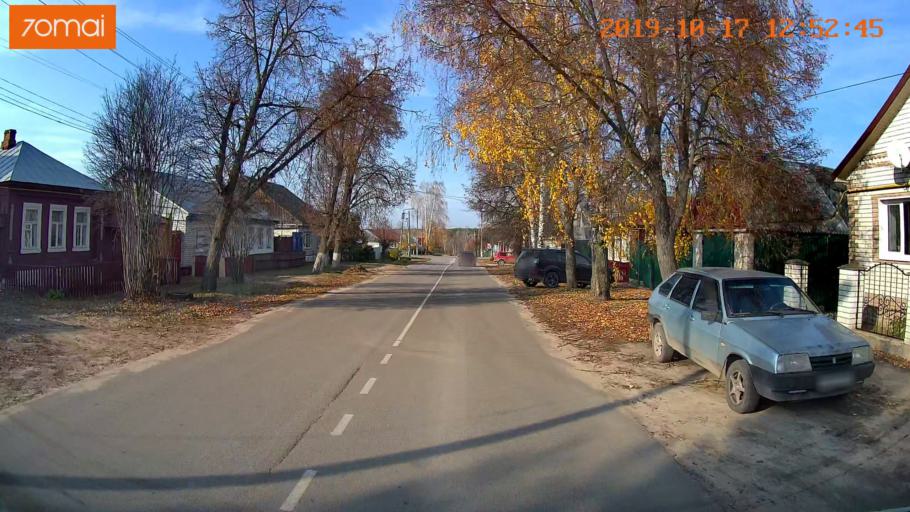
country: RU
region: Rjazan
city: Kasimov
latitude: 54.9438
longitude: 41.3873
